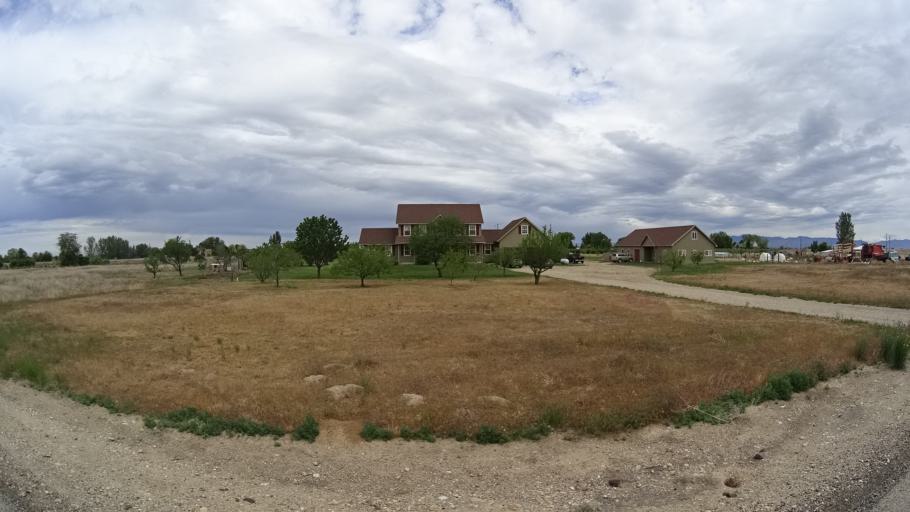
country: US
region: Idaho
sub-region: Ada County
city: Kuna
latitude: 43.4700
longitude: -116.4392
